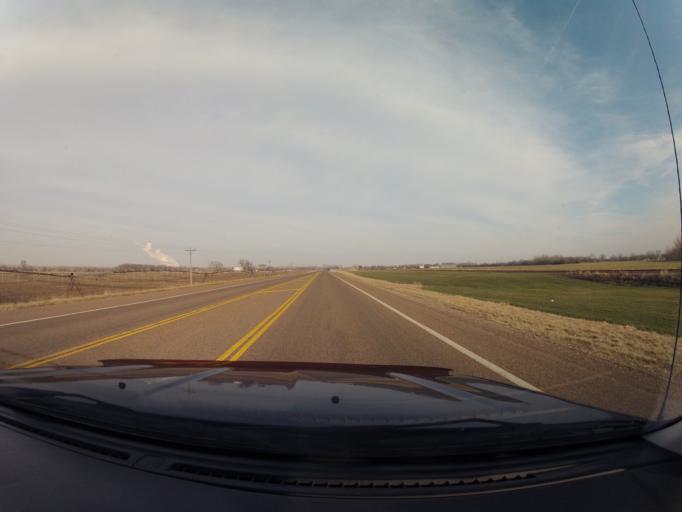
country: US
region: Kansas
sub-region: Pottawatomie County
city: Wamego
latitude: 39.2145
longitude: -96.2297
